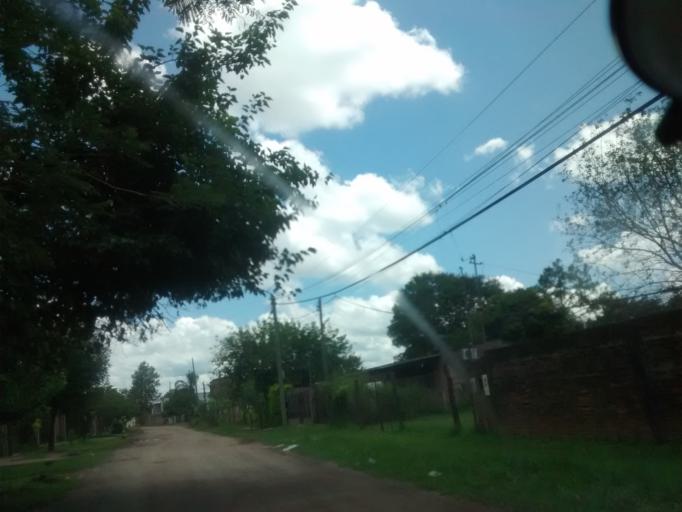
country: AR
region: Chaco
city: Resistencia
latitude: -27.4252
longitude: -58.9786
